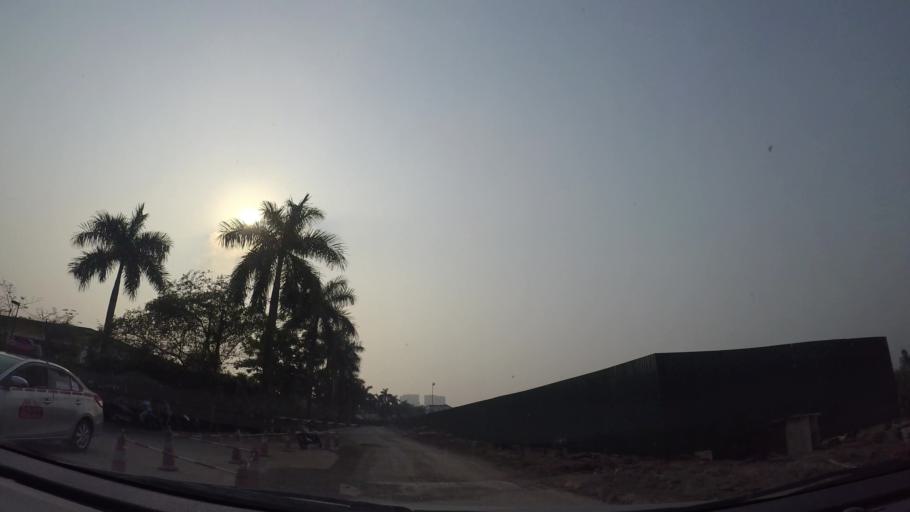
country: VN
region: Ha Noi
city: Tay Ho
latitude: 21.0756
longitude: 105.8094
